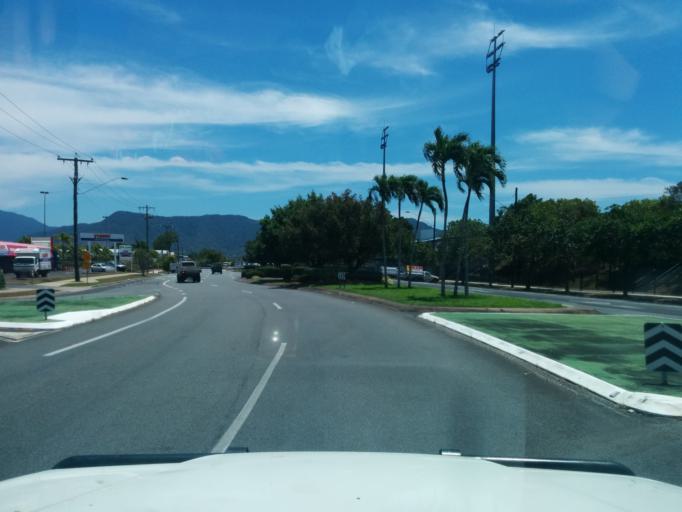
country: AU
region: Queensland
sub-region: Cairns
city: Cairns
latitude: -16.9305
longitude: 145.7688
